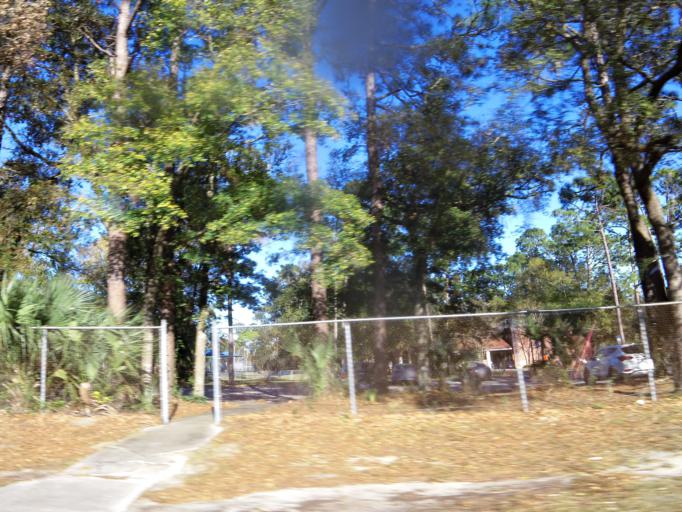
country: US
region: Florida
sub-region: Duval County
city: Jacksonville
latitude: 30.4597
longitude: -81.6331
